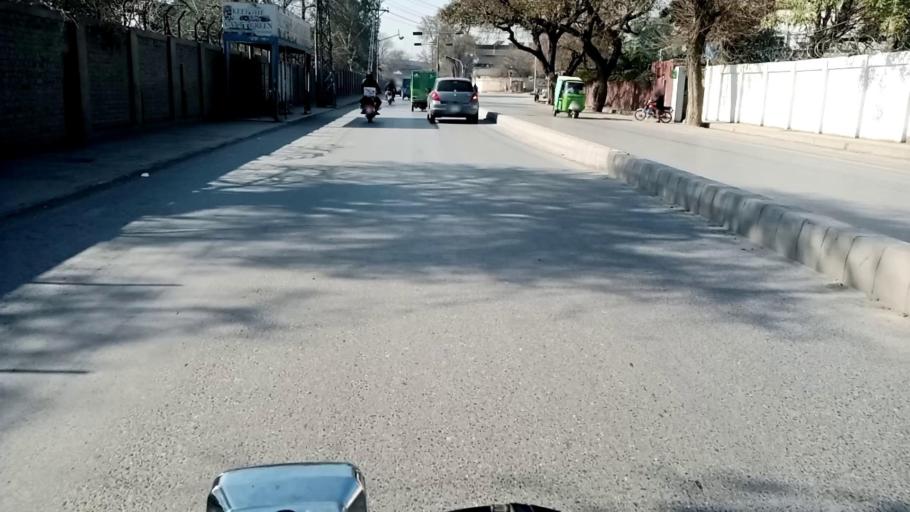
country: PK
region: Khyber Pakhtunkhwa
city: Peshawar
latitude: 34.0056
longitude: 71.5544
